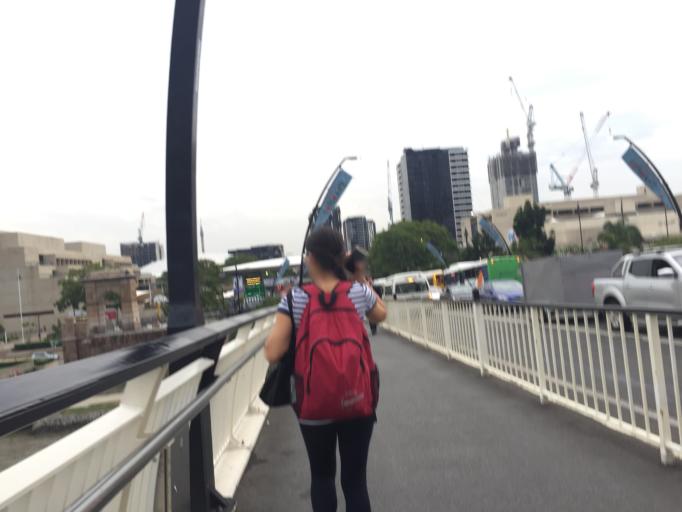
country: AU
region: Queensland
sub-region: Brisbane
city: South Brisbane
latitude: -27.4727
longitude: 153.0205
